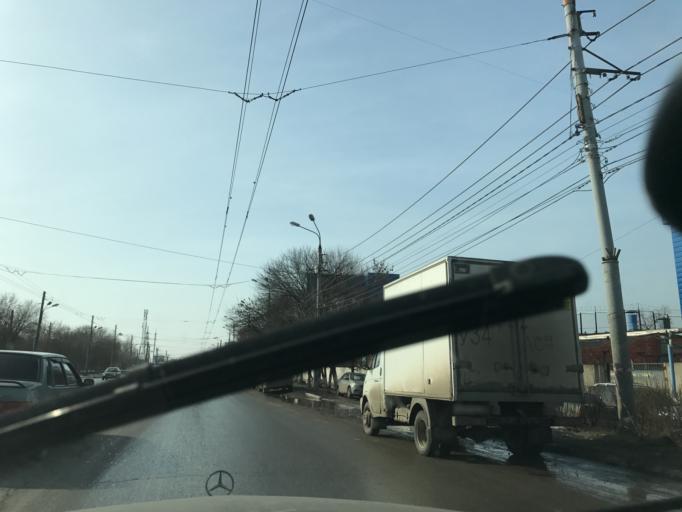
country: RU
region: Nizjnij Novgorod
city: Nizhniy Novgorod
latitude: 56.2663
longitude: 43.9096
